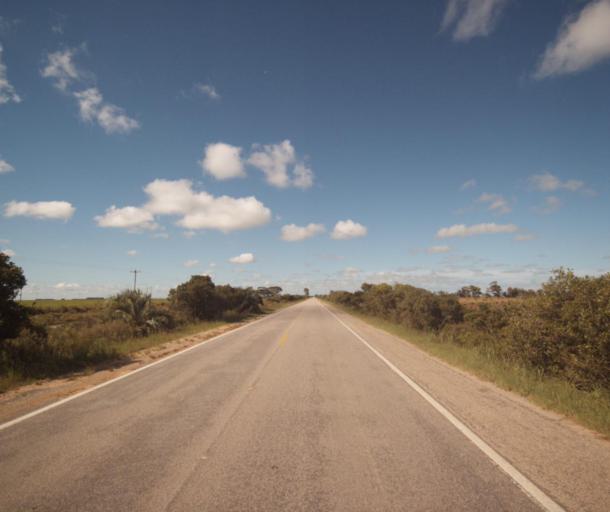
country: BR
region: Rio Grande do Sul
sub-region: Santa Vitoria Do Palmar
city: Santa Vitoria do Palmar
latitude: -33.3847
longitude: -53.2019
